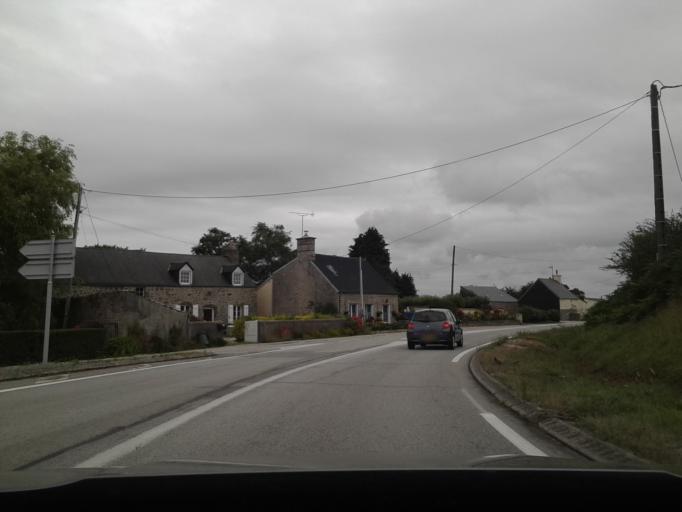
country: FR
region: Lower Normandy
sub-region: Departement de la Manche
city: Valognes
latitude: 49.5196
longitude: -1.4967
